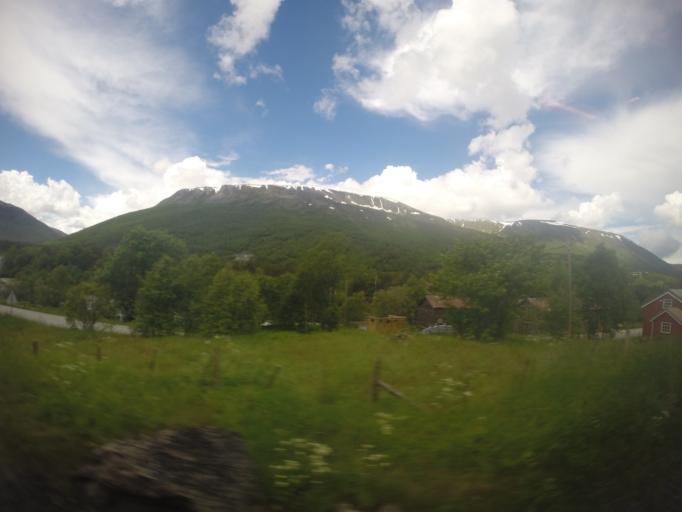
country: NO
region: Sor-Trondelag
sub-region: Oppdal
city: Oppdal
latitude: 62.5085
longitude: 9.5988
